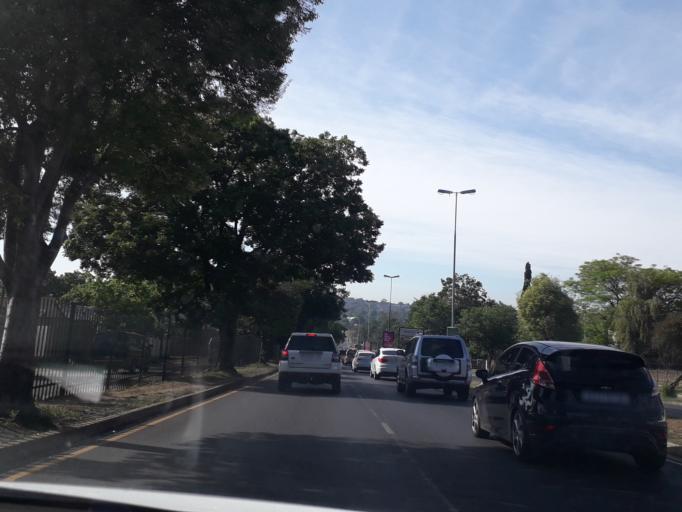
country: ZA
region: Gauteng
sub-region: City of Johannesburg Metropolitan Municipality
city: Johannesburg
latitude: -26.1072
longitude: 28.0162
